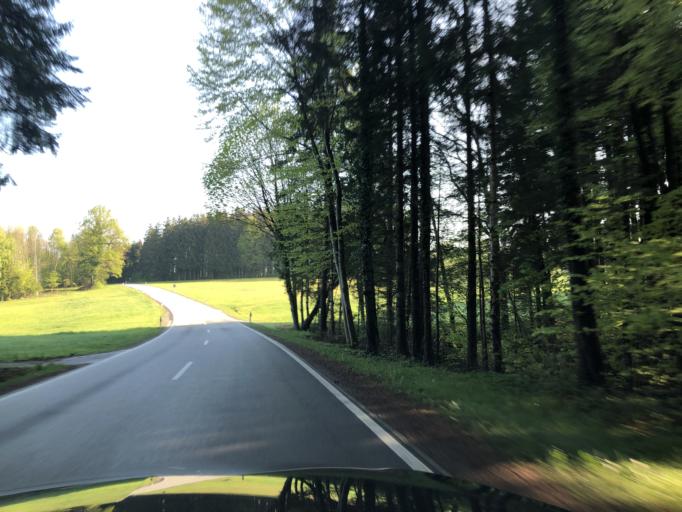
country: DE
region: Bavaria
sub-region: Upper Bavaria
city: Frasdorf
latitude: 47.8225
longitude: 12.2572
